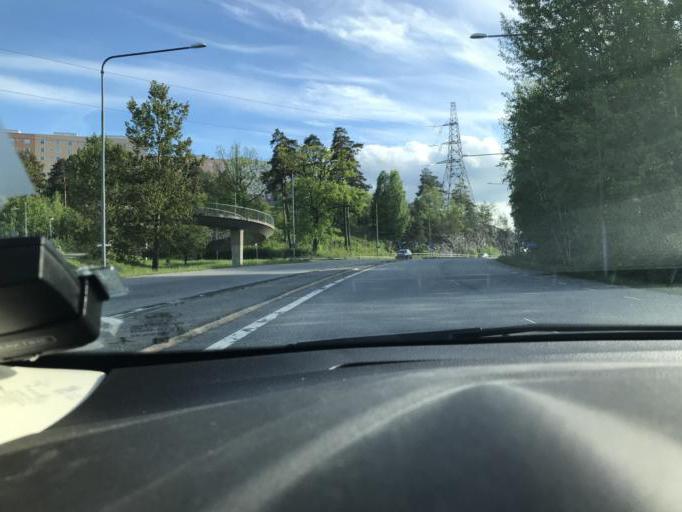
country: SE
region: Stockholm
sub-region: Botkyrka Kommun
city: Alby
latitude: 59.2446
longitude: 17.8418
